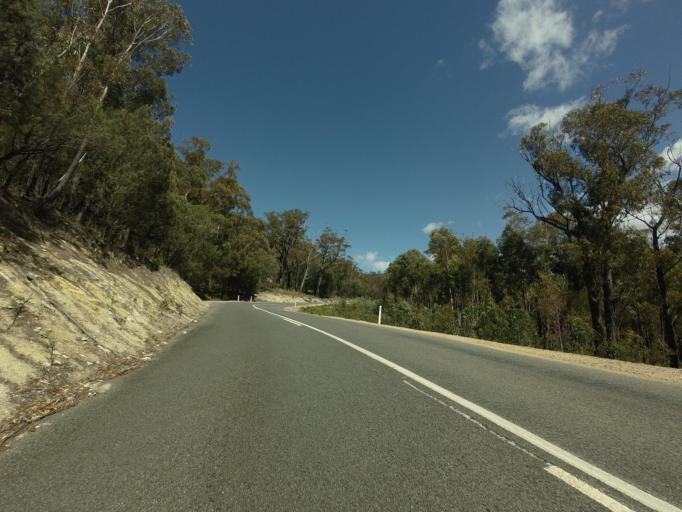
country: AU
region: Tasmania
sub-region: Break O'Day
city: St Helens
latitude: -41.6619
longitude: 148.2703
